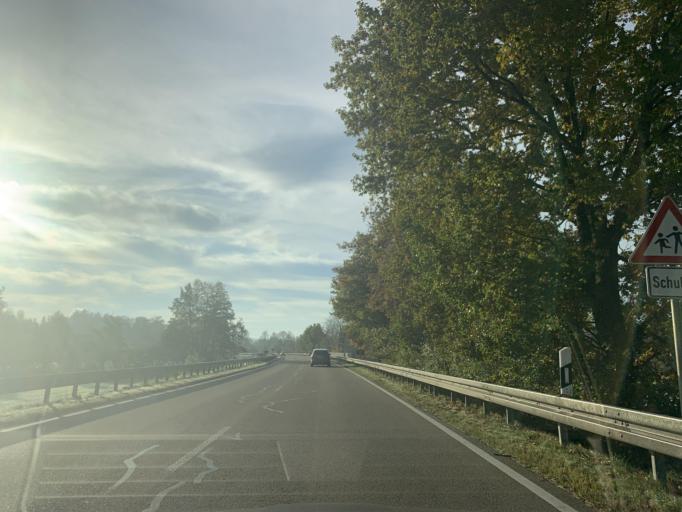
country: DE
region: Bavaria
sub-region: Upper Palatinate
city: Neunburg vorm Wald
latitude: 49.3566
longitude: 12.3747
